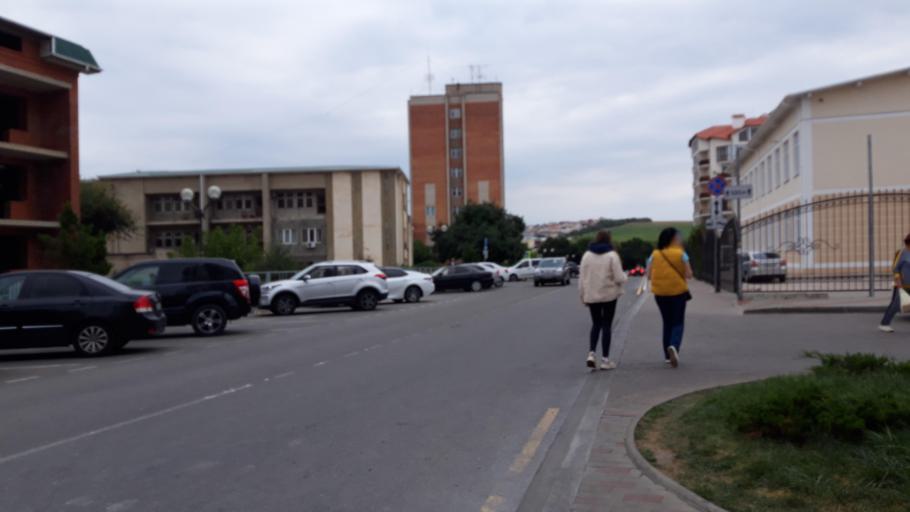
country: RU
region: Krasnodarskiy
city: Gelendzhik
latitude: 44.5514
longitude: 38.0595
